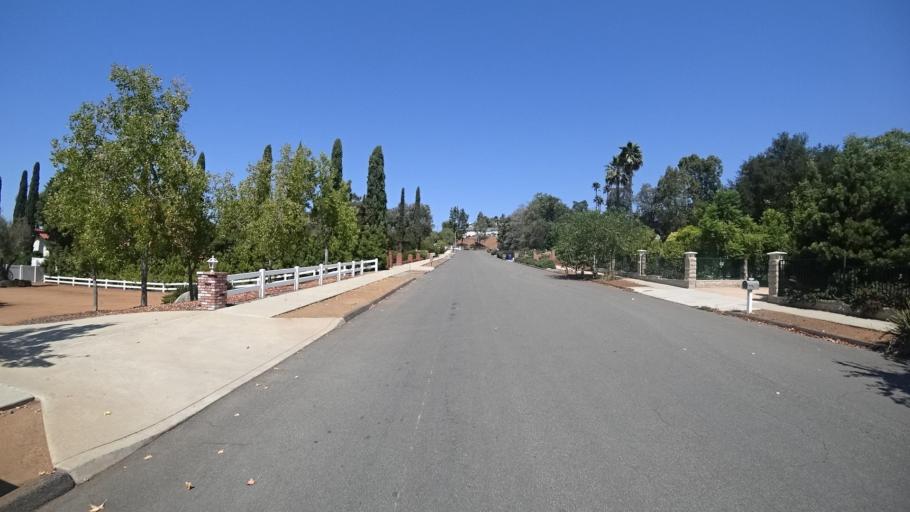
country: US
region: California
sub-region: San Diego County
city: Vista
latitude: 33.1881
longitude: -117.1971
